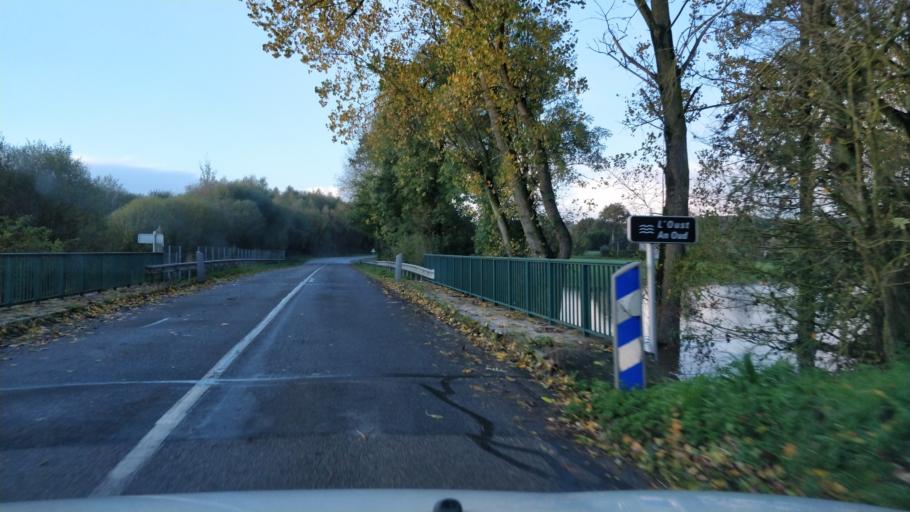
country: FR
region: Brittany
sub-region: Departement du Morbihan
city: Saint-Gonnery
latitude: 48.1363
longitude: -2.7975
